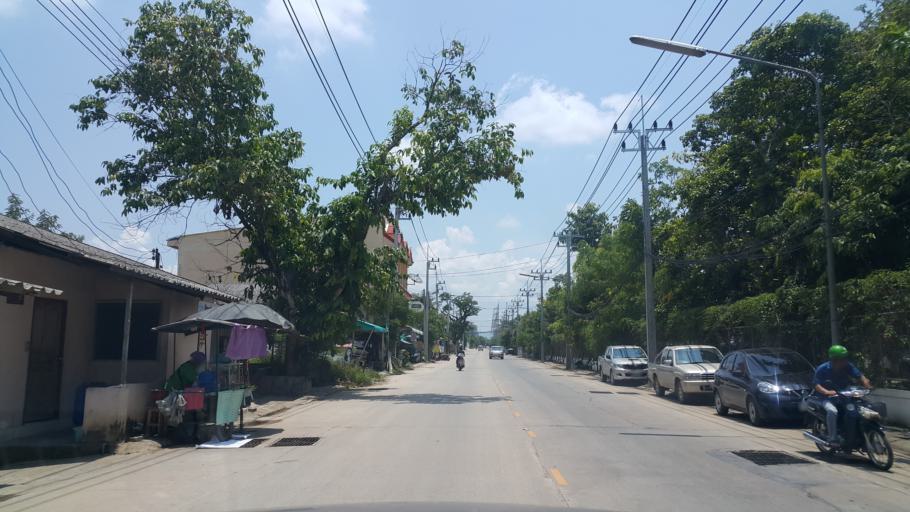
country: TH
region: Chiang Rai
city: Chiang Rai
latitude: 19.9142
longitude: 99.8218
